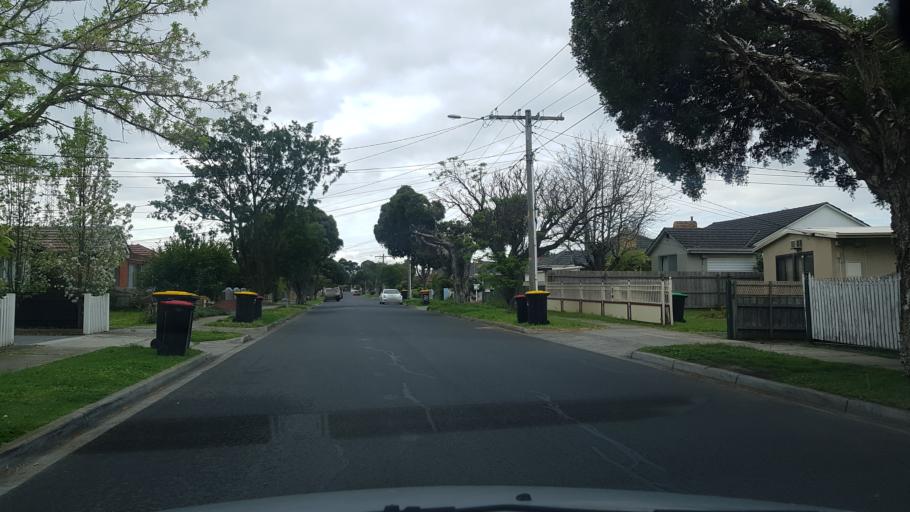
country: AU
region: Victoria
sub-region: Greater Dandenong
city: Springvale
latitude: -37.9394
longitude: 145.1457
